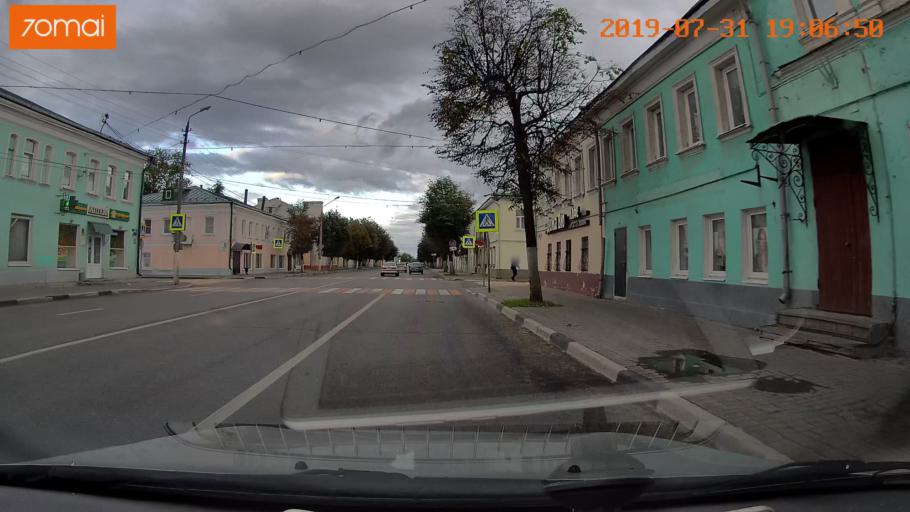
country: RU
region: Moskovskaya
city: Kolomna
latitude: 55.1004
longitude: 38.7567
